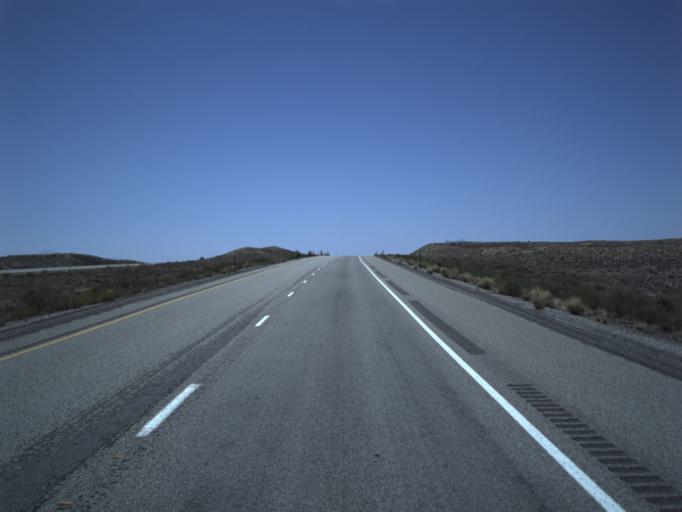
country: US
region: Utah
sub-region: Grand County
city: Moab
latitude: 39.0089
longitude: -109.3100
